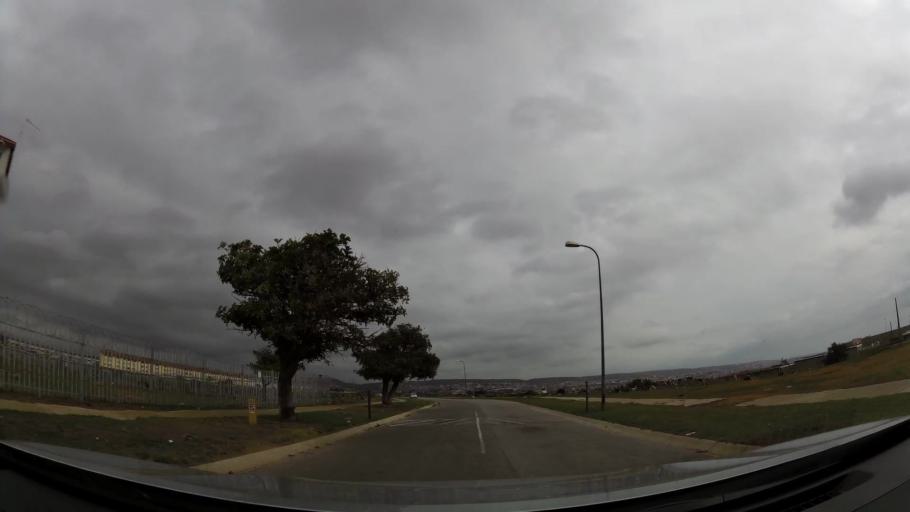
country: ZA
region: Eastern Cape
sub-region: Nelson Mandela Bay Metropolitan Municipality
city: Port Elizabeth
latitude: -33.8885
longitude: 25.5604
